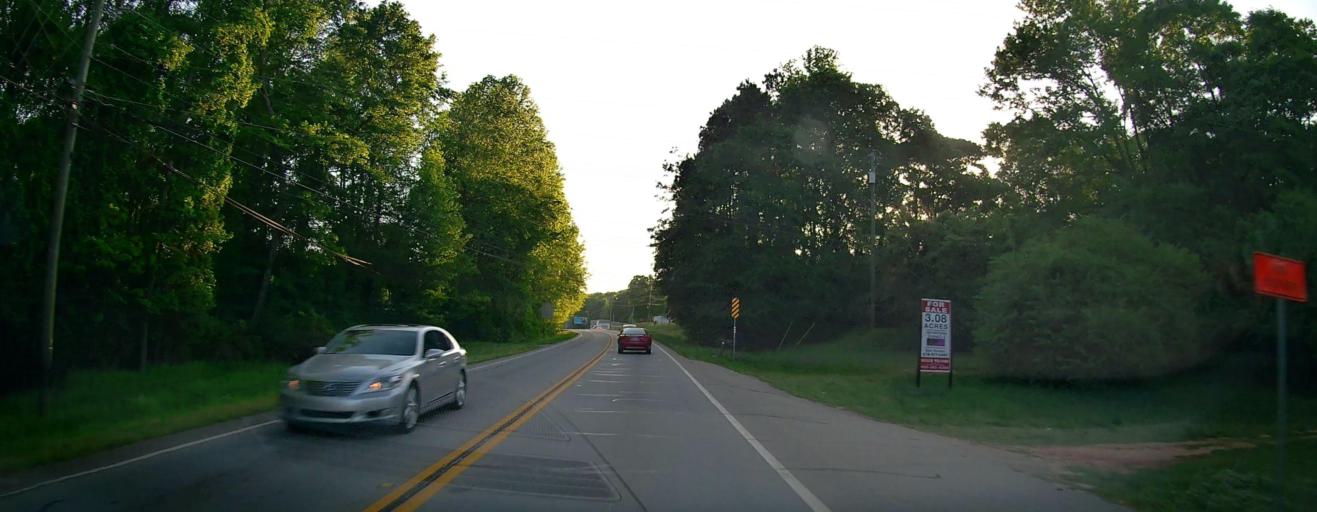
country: US
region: Georgia
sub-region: Newton County
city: Porterdale
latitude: 33.5649
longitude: -83.9055
